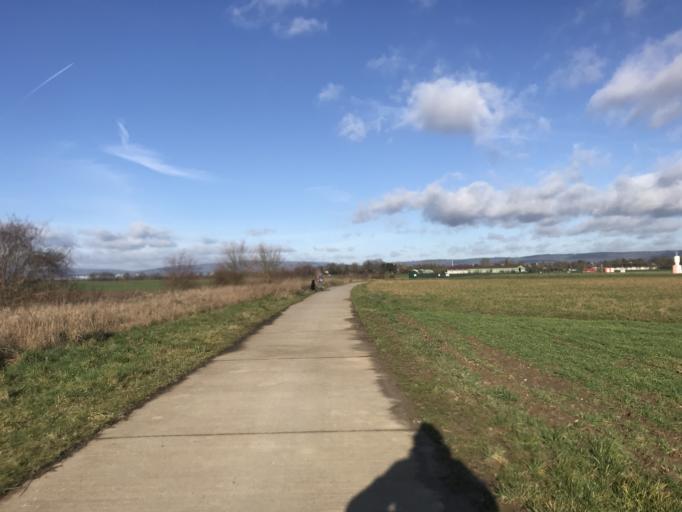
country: DE
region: Hesse
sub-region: Regierungsbezirk Darmstadt
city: Hochheim am Main
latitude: 50.0442
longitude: 8.3119
